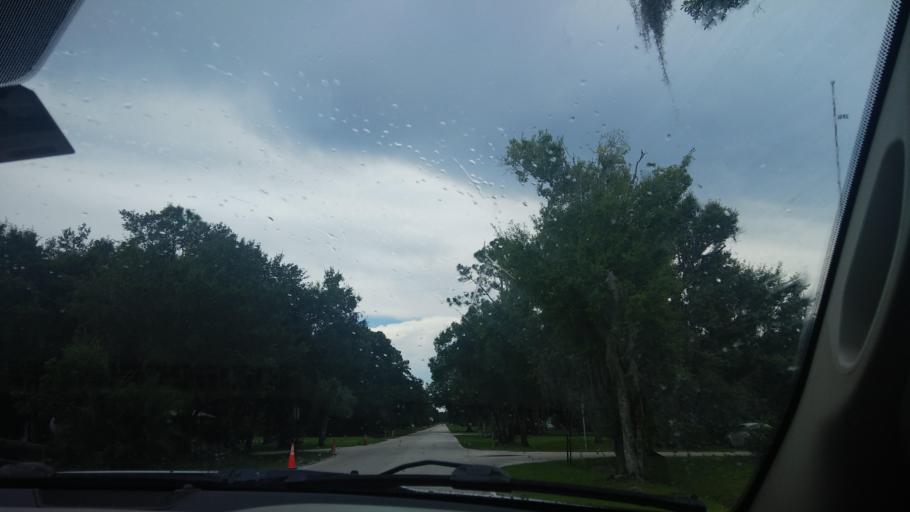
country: US
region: Florida
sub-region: Indian River County
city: Fellsmere
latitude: 27.7665
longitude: -80.6013
